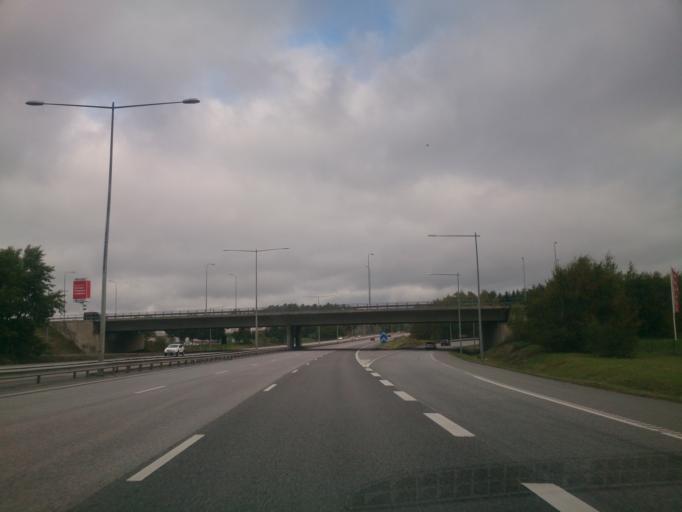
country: SE
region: Stockholm
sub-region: Haninge Kommun
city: Handen
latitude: 59.1994
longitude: 18.1328
